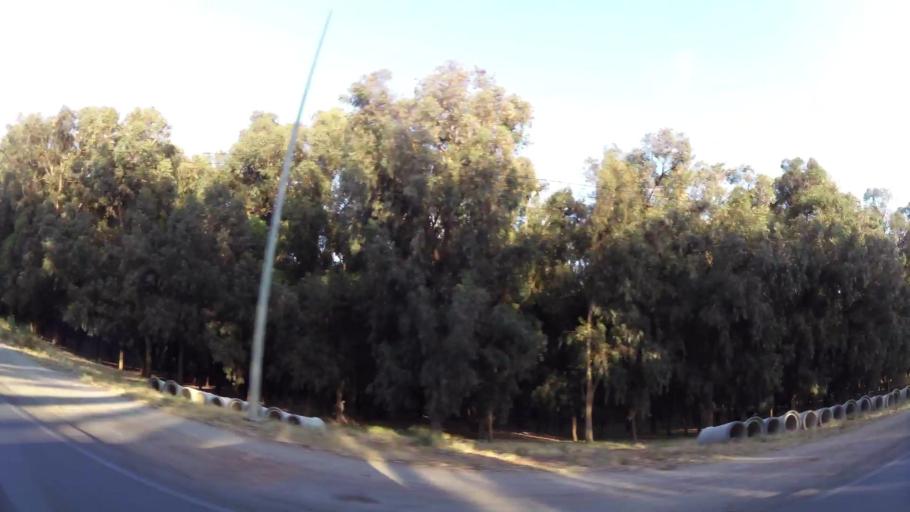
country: MA
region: Rabat-Sale-Zemmour-Zaer
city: Sale
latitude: 34.1314
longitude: -6.7323
